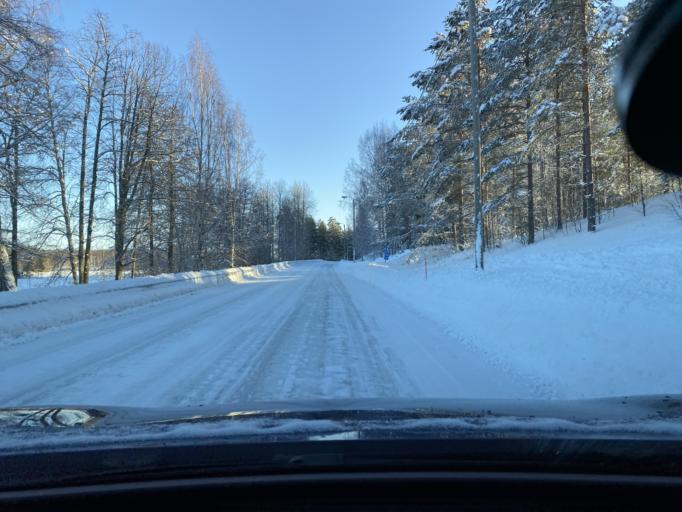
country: FI
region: Southern Savonia
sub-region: Mikkeli
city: Kangasniemi
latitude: 62.0128
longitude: 26.6182
